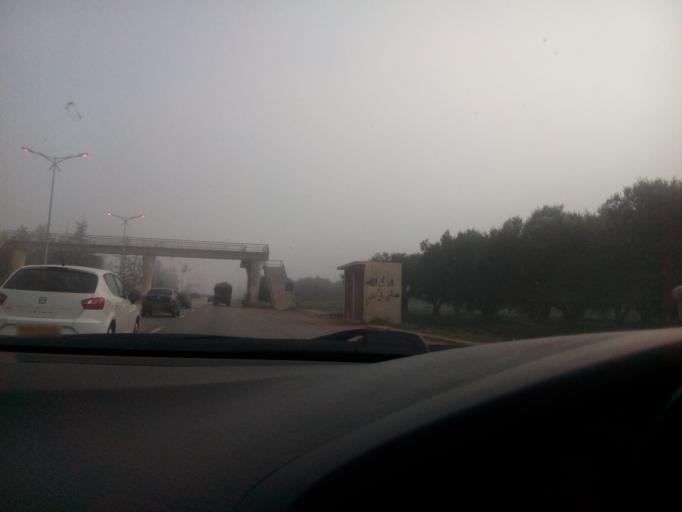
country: DZ
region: Oran
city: Bou Tlelis
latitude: 35.5884
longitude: -0.8053
